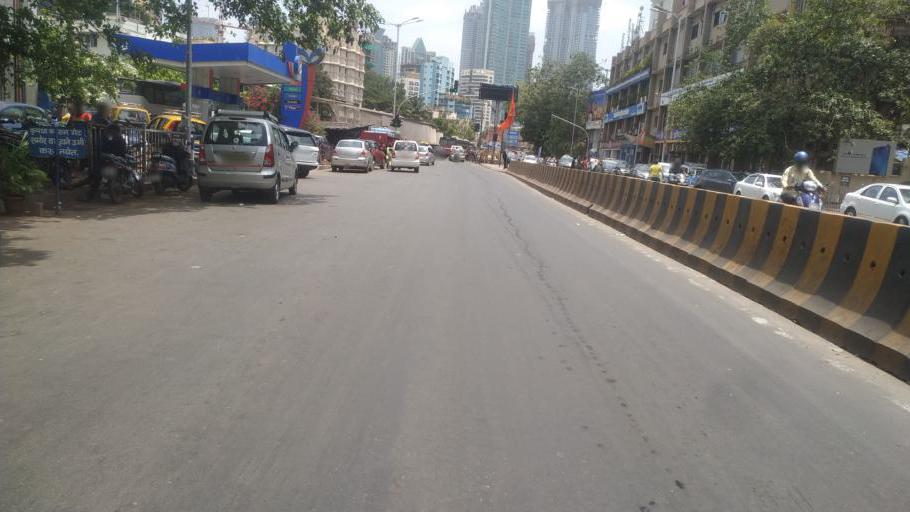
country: IN
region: Maharashtra
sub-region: Mumbai Suburban
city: Mumbai
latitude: 19.0181
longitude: 72.8310
